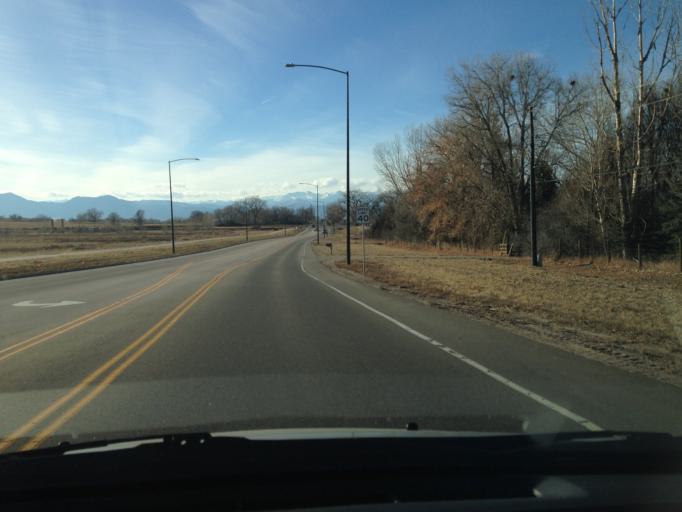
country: US
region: Colorado
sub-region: Boulder County
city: Erie
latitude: 40.0365
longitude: -105.0881
